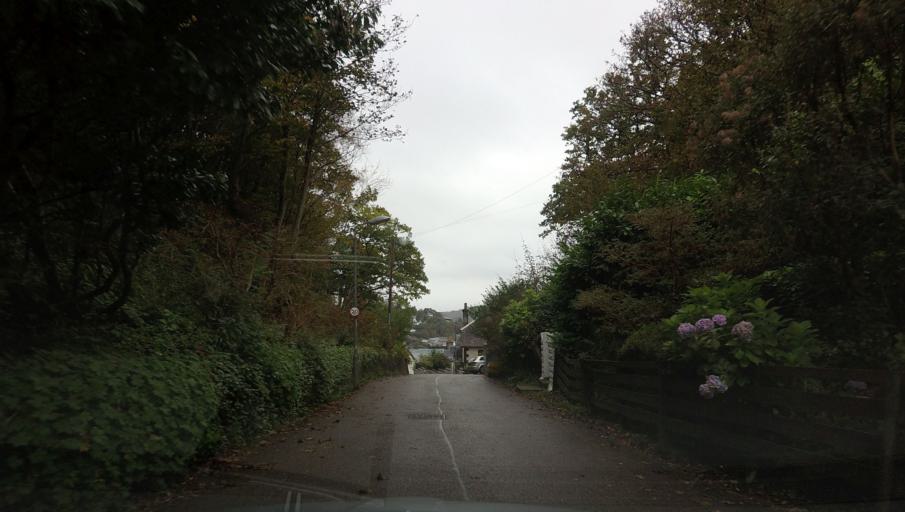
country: GB
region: Scotland
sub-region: Argyll and Bute
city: Oban
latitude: 56.4162
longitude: -5.4692
